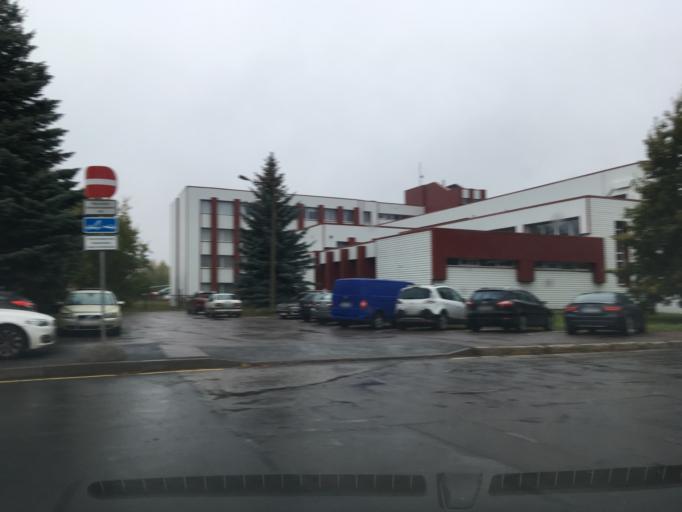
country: EE
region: Harju
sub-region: Tallinna linn
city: Kose
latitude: 59.4550
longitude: 24.8437
